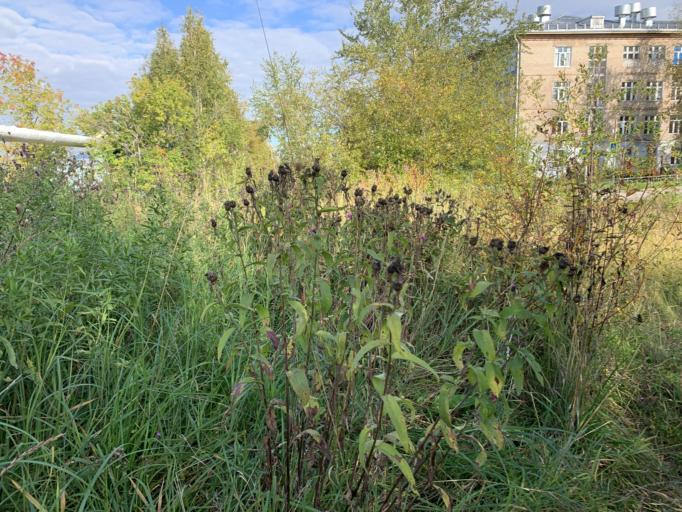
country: RU
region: Perm
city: Gubakha
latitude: 58.8376
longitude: 57.5588
